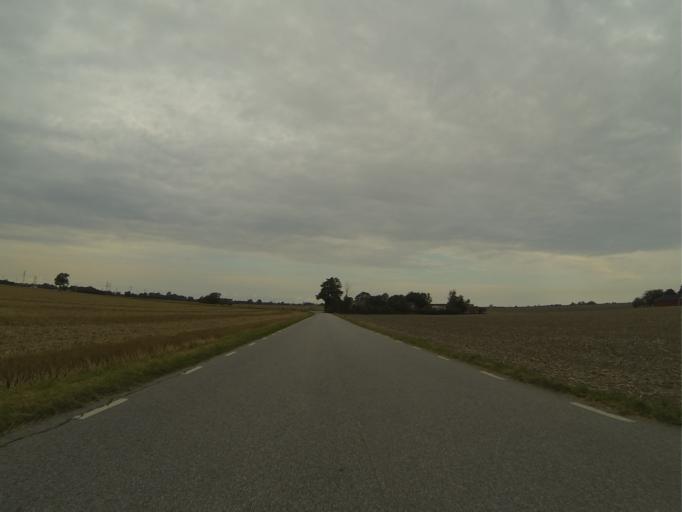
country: SE
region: Skane
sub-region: Staffanstorps Kommun
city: Hjaerup
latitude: 55.6552
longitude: 13.1591
